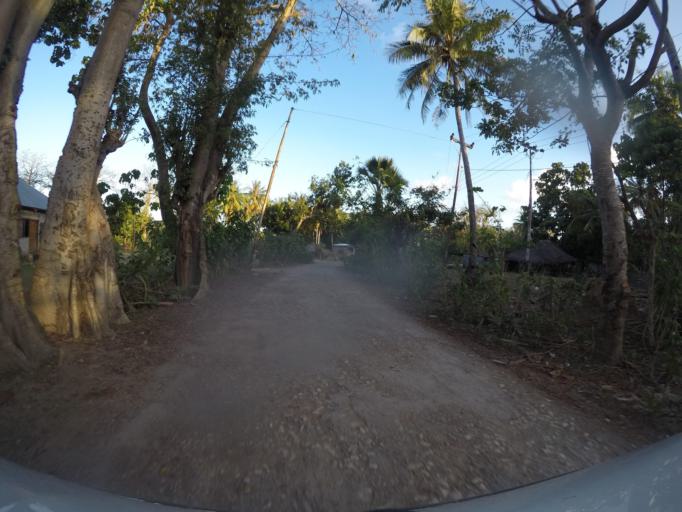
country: TL
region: Baucau
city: Venilale
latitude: -8.7427
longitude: 126.7144
